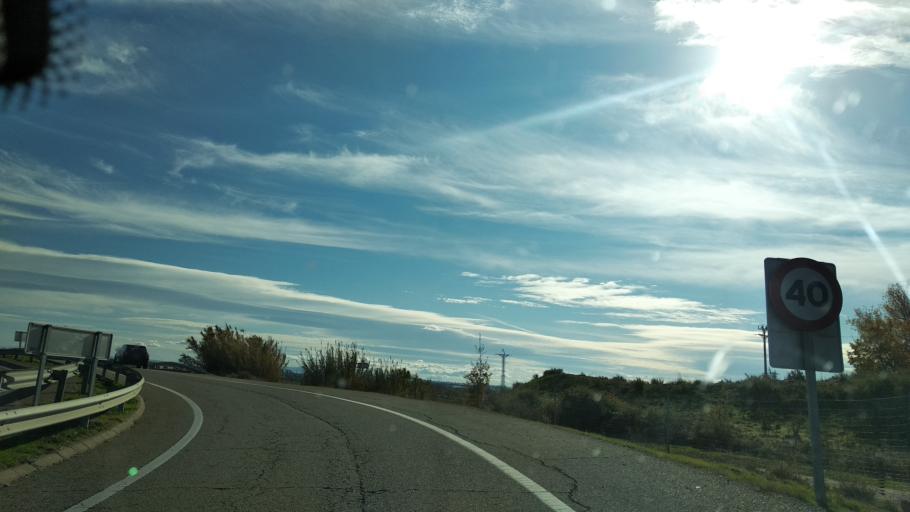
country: ES
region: Catalonia
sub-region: Provincia de Lleida
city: Alcoletge
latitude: 41.6563
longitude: 0.6568
